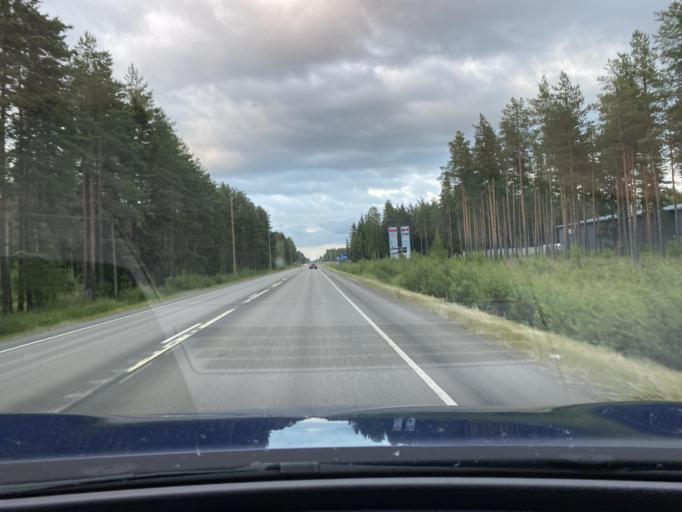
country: FI
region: Northern Ostrobothnia
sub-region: Ylivieska
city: Kalajoki
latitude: 64.2466
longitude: 23.8791
